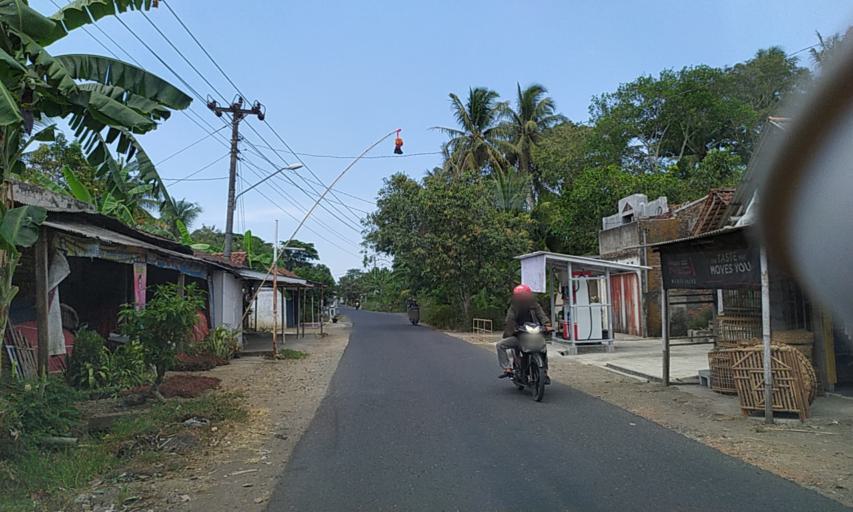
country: ID
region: Central Java
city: Tinggarmalang
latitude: -7.5987
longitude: 109.1989
